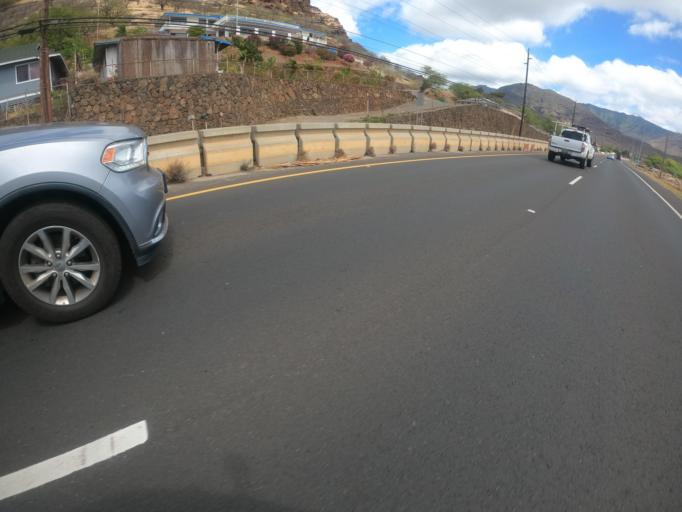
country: US
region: Hawaii
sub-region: Honolulu County
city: Nanakuli
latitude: 21.3980
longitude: -158.1682
